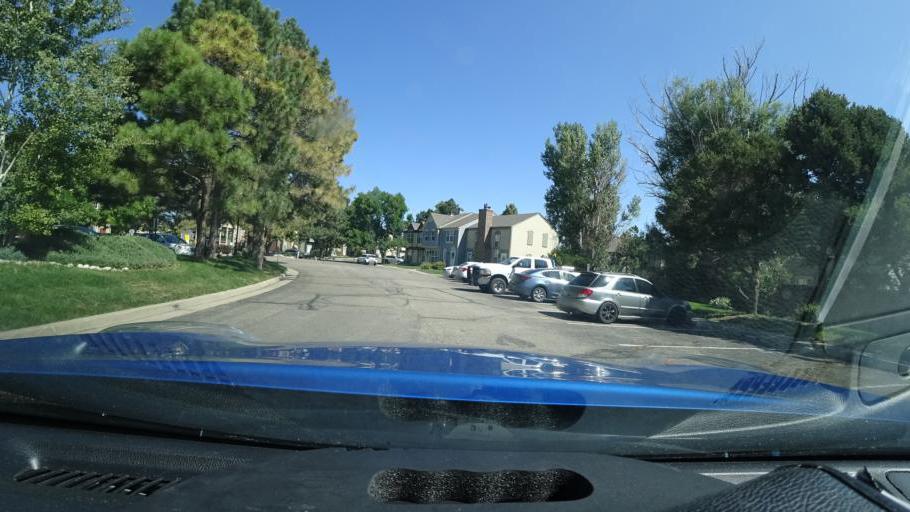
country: US
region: Colorado
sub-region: Adams County
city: Aurora
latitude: 39.6851
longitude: -104.8234
